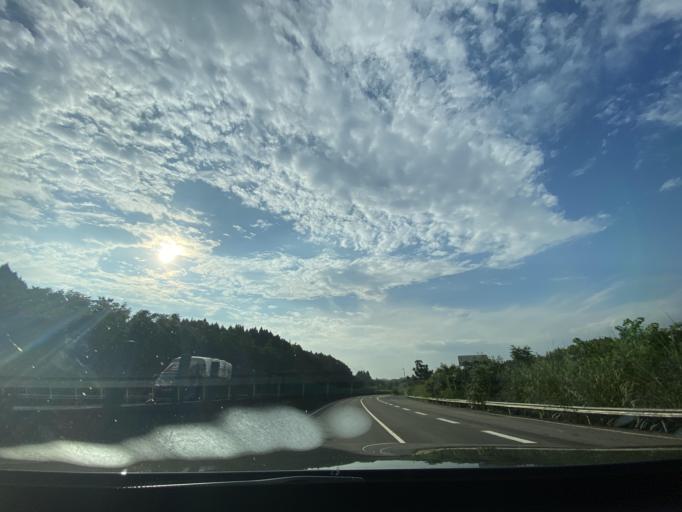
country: CN
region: Sichuan
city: Jiancheng
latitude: 30.2778
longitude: 104.5924
